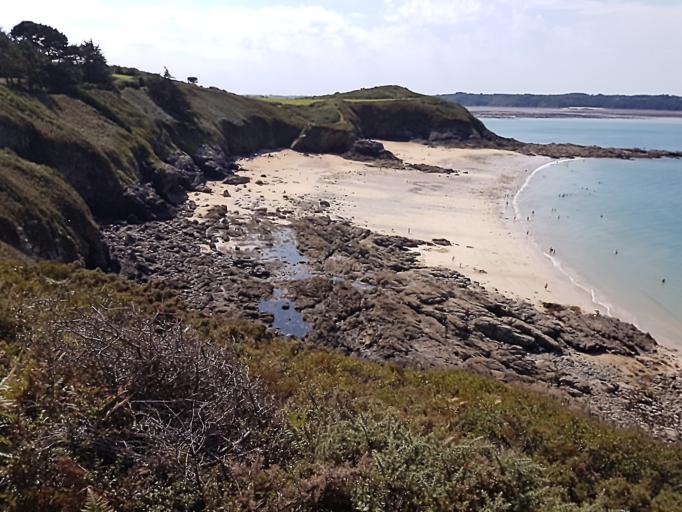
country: FR
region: Brittany
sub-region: Departement des Cotes-d'Armor
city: Saint-Cast-le-Guildo
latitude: 48.6421
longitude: -2.2645
